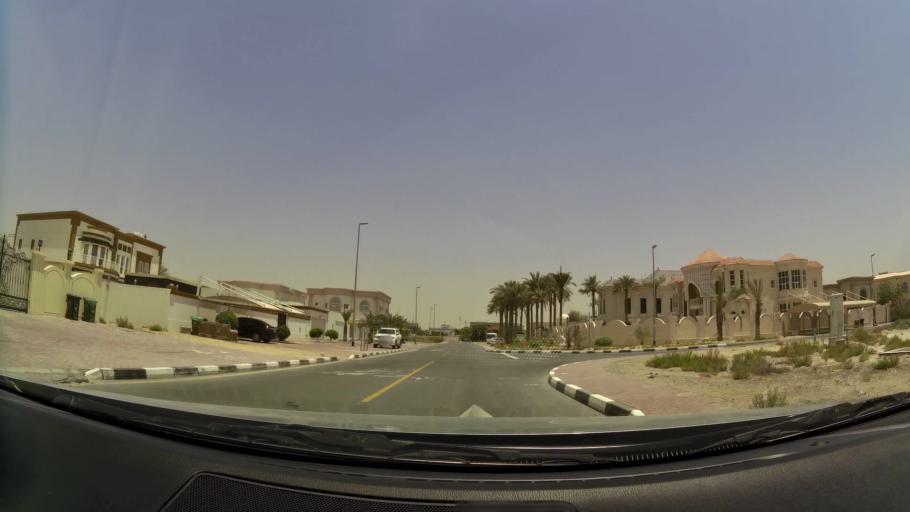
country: AE
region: Dubai
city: Dubai
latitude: 25.0968
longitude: 55.1916
